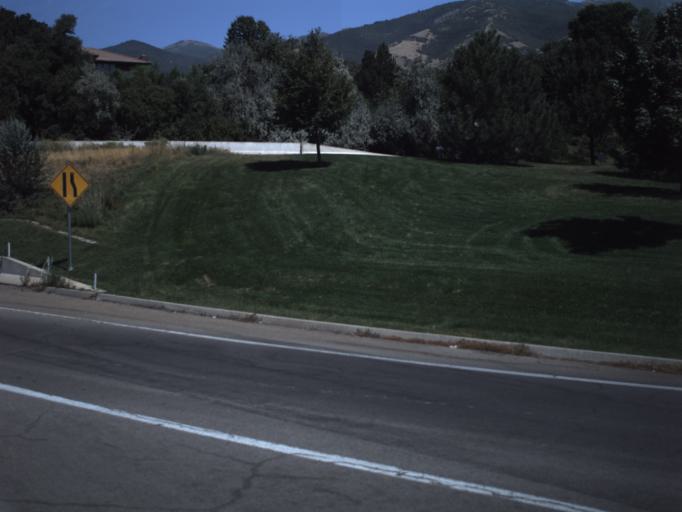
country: US
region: Utah
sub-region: Davis County
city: Fruit Heights
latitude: 41.0113
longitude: -111.9114
